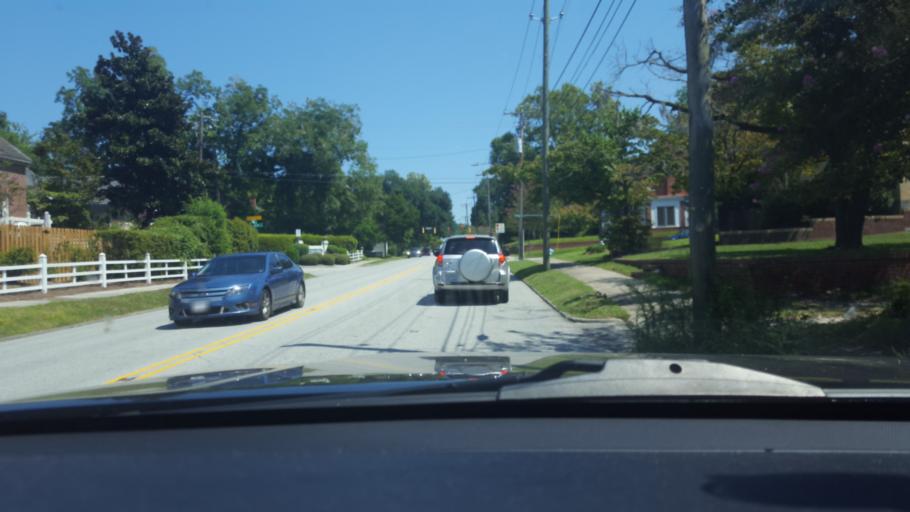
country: US
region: North Carolina
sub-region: New Hanover County
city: Wilmington
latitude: 34.2378
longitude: -77.9199
